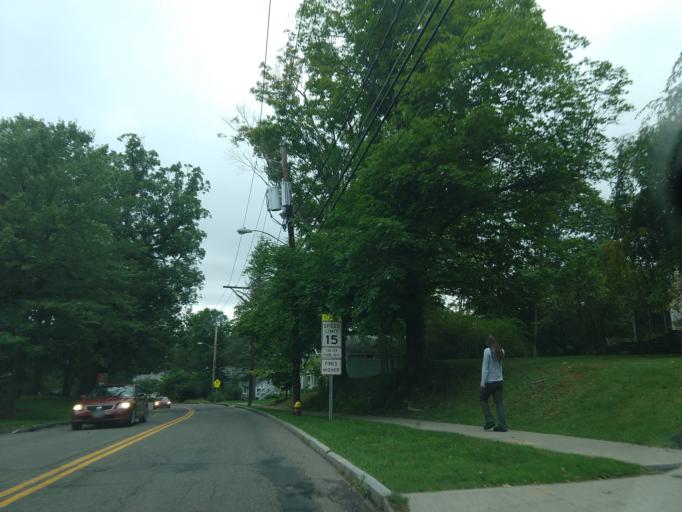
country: US
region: New York
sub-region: Tompkins County
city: South Hill
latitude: 42.4325
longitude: -76.4917
